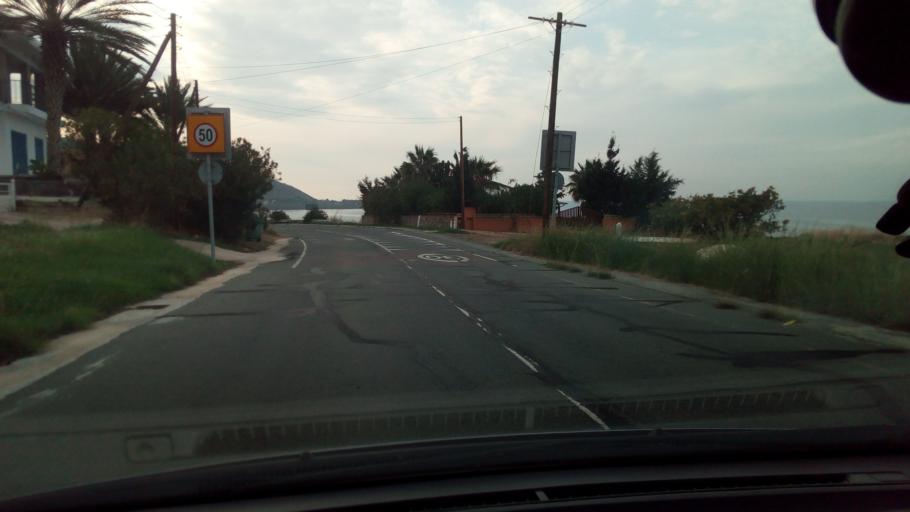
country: CY
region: Lefkosia
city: Kato Pyrgos
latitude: 35.1712
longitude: 32.5792
